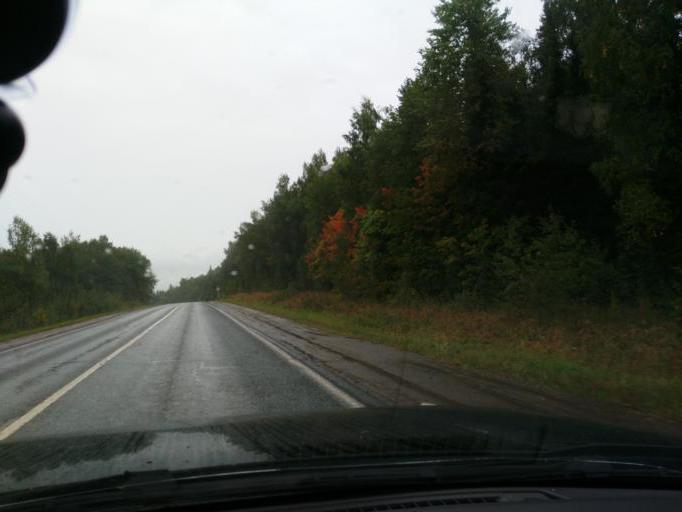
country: RU
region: Perm
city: Yugo-Kamskiy
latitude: 57.5813
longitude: 55.6777
